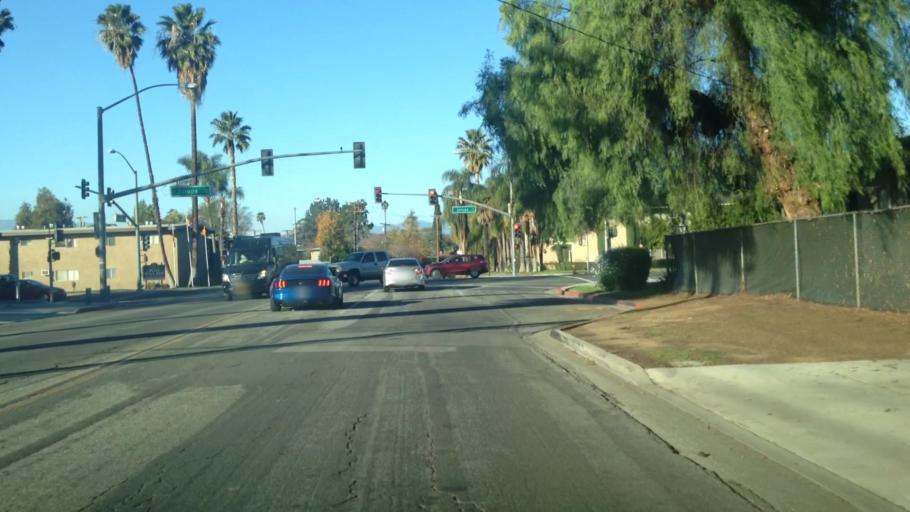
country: US
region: California
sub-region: Riverside County
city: Riverside
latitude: 33.9605
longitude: -117.4011
